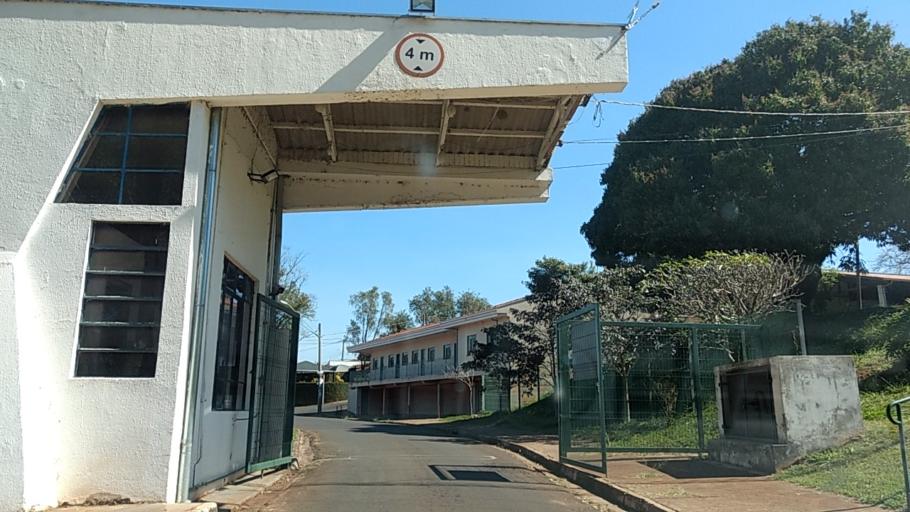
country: BR
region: Sao Paulo
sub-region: Botucatu
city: Botucatu
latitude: -22.8577
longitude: -48.4340
